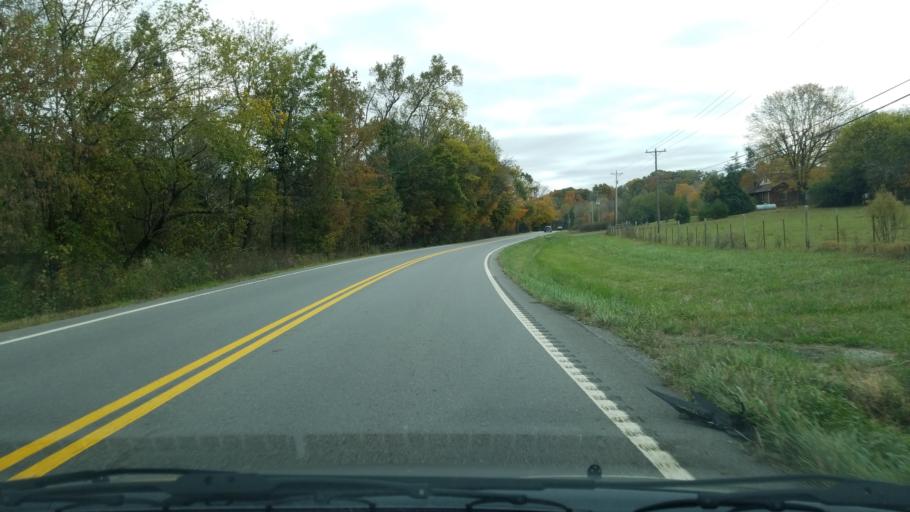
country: US
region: Tennessee
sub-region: Bradley County
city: Hopewell
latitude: 35.3350
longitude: -84.9716
